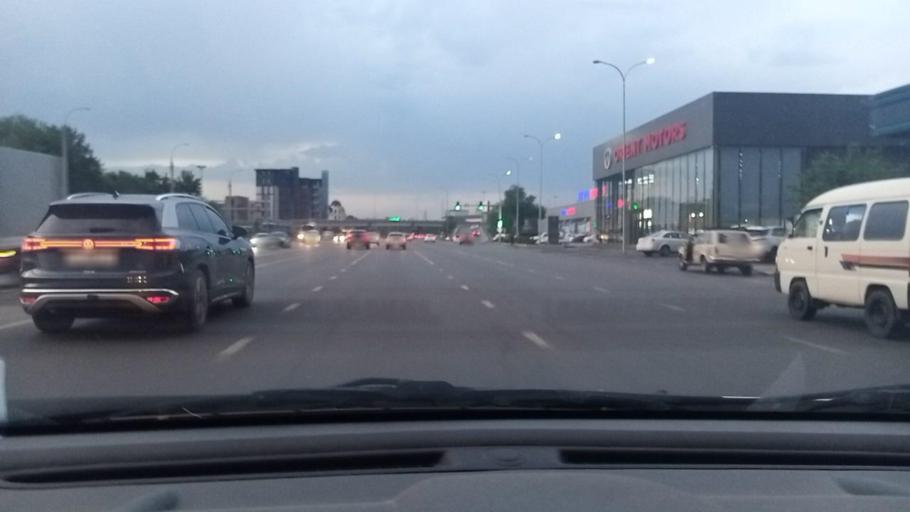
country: UZ
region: Toshkent Shahri
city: Tashkent
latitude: 41.2946
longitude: 69.2907
